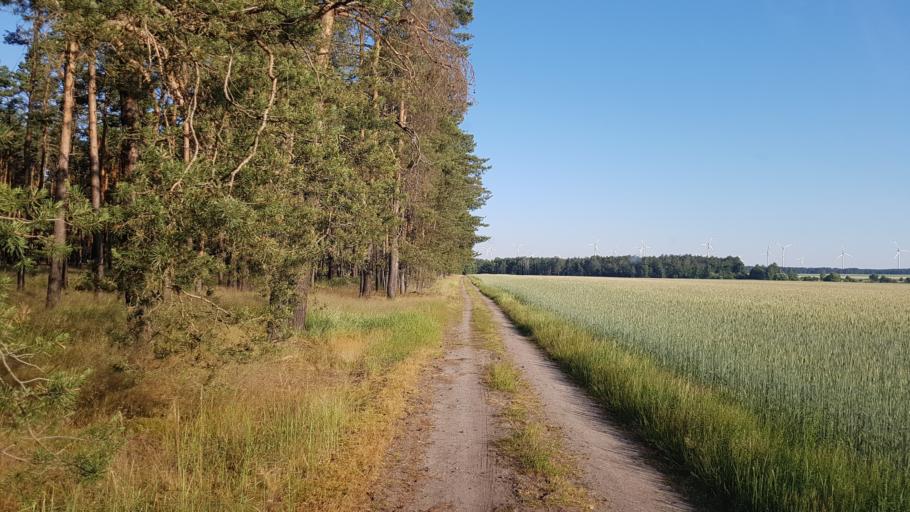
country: DE
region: Brandenburg
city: Schilda
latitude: 51.6349
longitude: 13.4059
